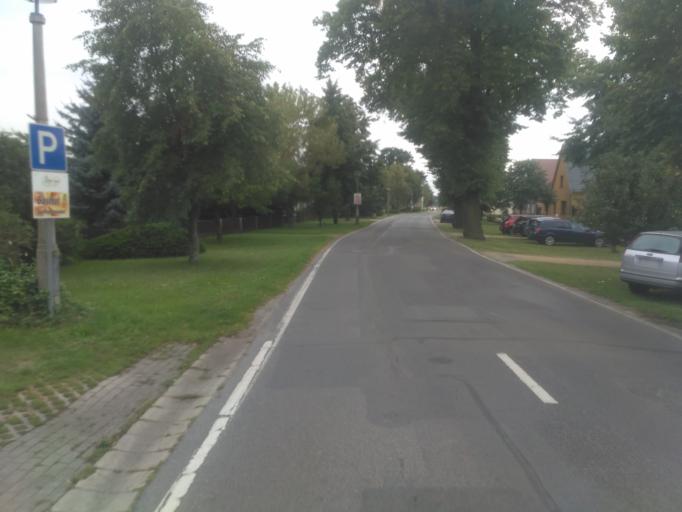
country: DE
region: Brandenburg
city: Welzow
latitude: 51.4940
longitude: 14.1224
